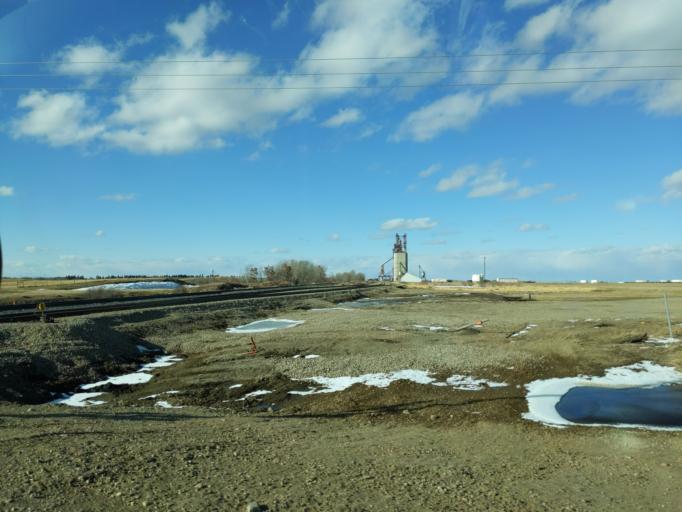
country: CA
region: Saskatchewan
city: Lloydminster
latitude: 53.2489
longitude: -109.9665
